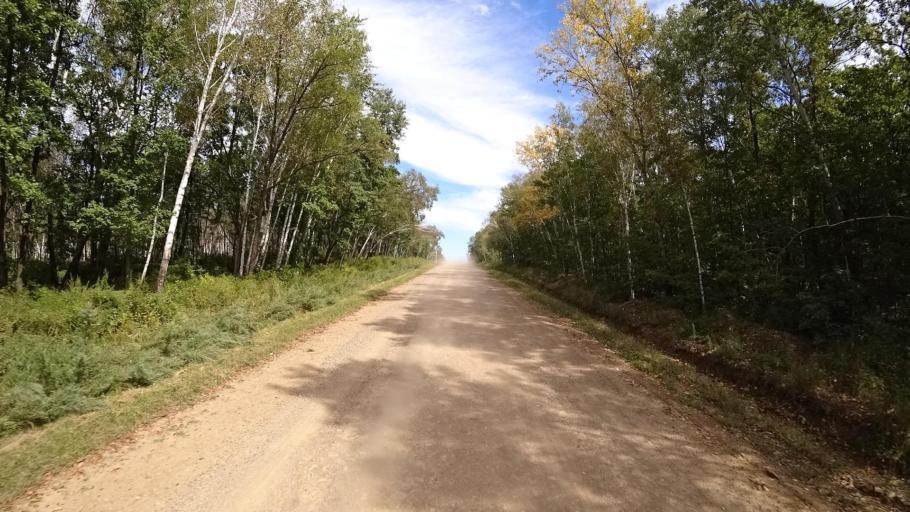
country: RU
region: Primorskiy
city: Yakovlevka
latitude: 44.6965
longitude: 133.6218
